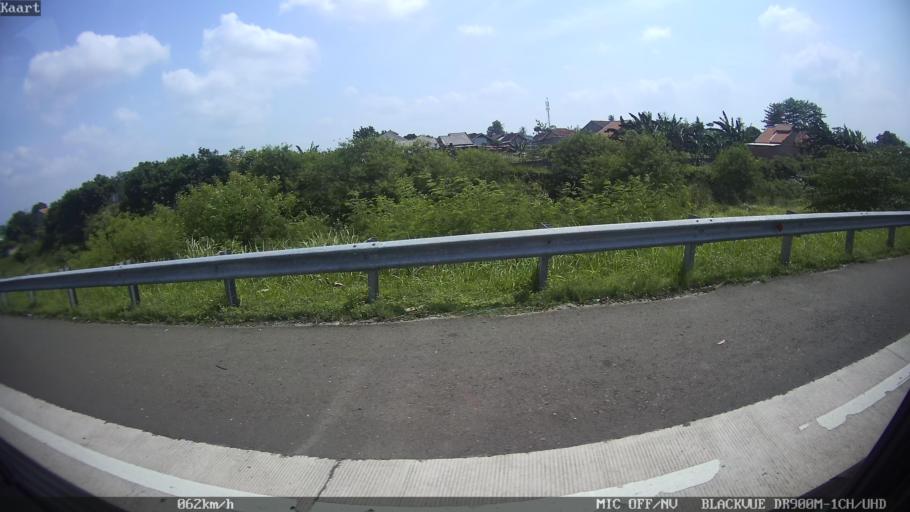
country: ID
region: Lampung
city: Kedaton
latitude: -5.3288
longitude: 105.2868
